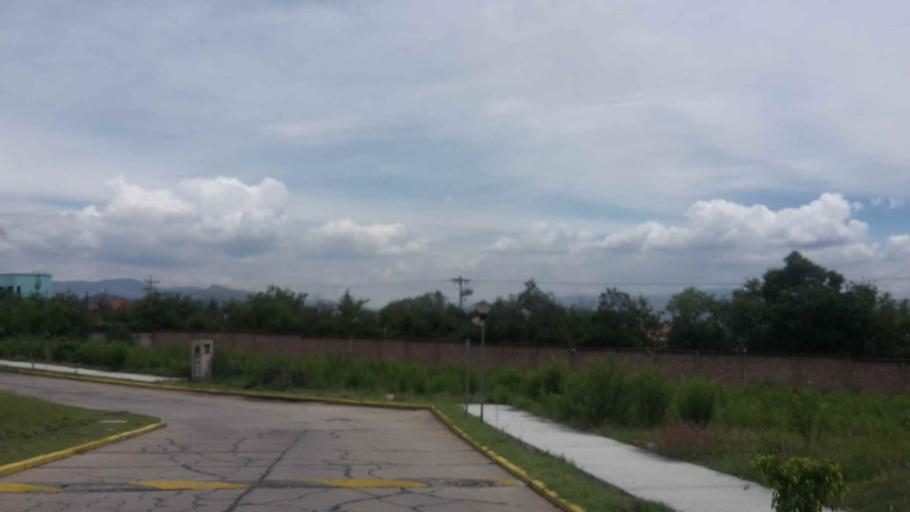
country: BO
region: Cochabamba
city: Cochabamba
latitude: -17.3421
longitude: -66.1865
